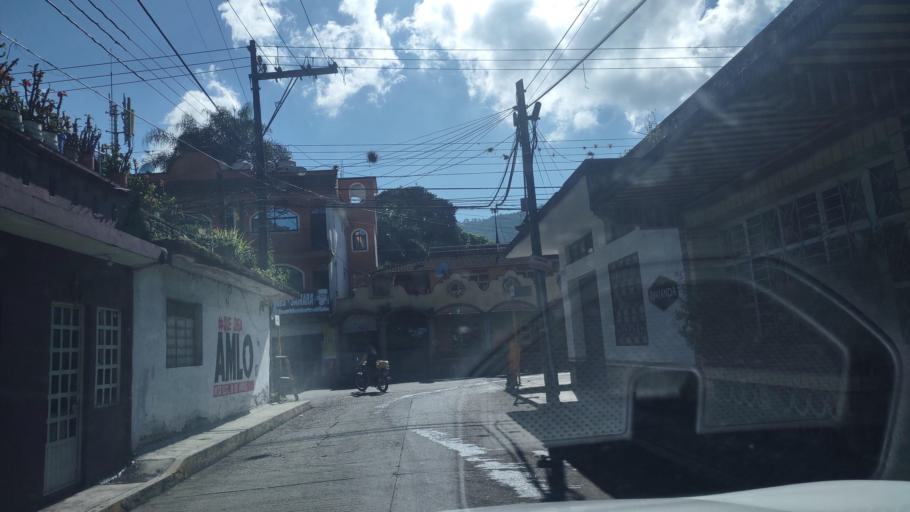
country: MX
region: Veracruz
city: Cuautlapan
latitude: 18.8729
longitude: -97.0221
